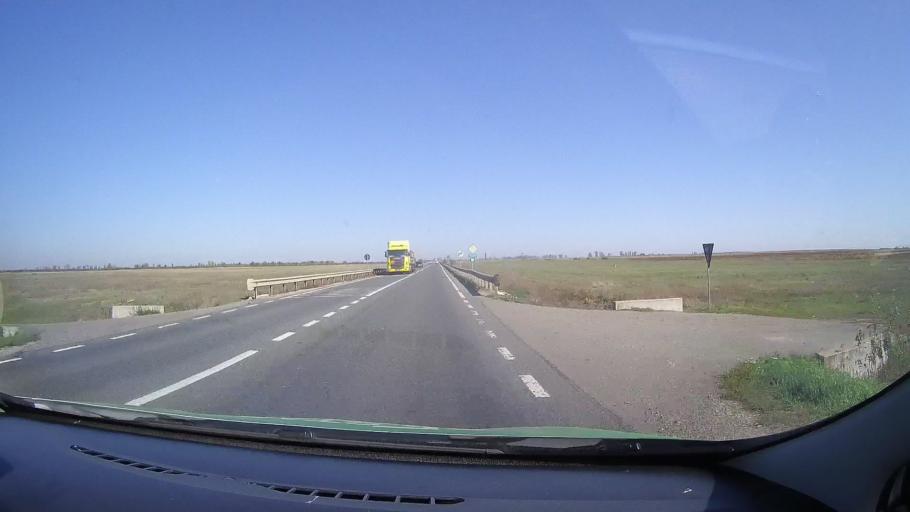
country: RO
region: Satu Mare
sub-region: Comuna Moftinu
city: Moftinu Mic
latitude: 47.6884
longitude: 22.6092
